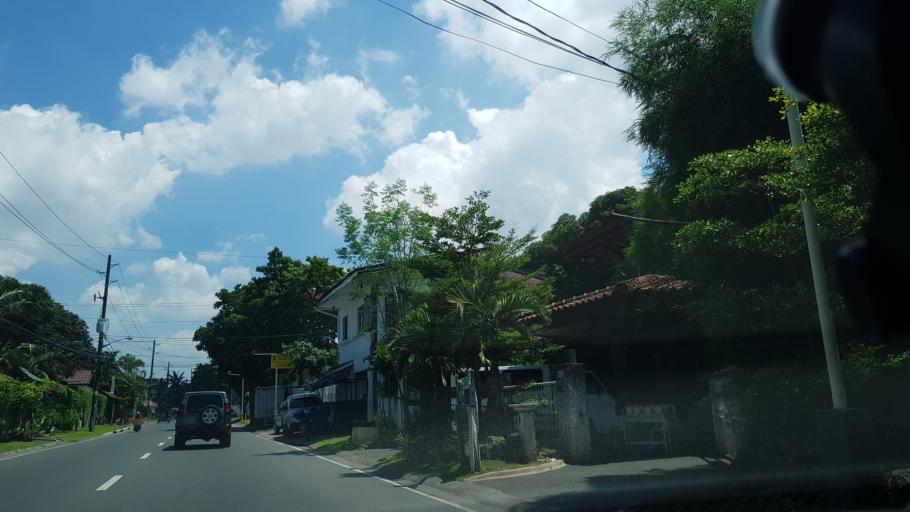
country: PH
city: Sambayanihan People's Village
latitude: 14.4518
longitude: 120.9979
